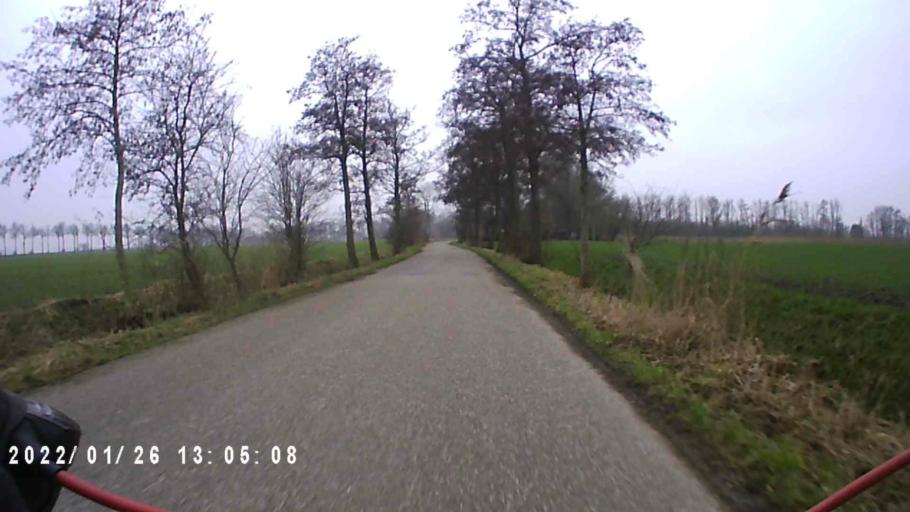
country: NL
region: Groningen
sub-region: Gemeente Zuidhorn
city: Oldehove
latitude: 53.3542
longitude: 6.4395
